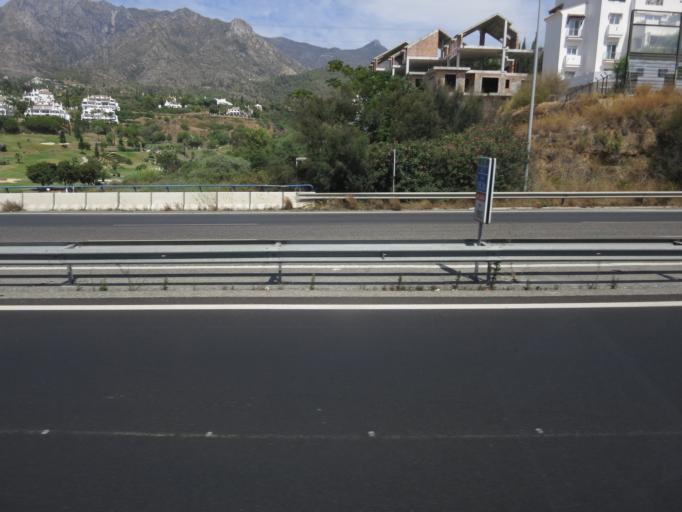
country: ES
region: Andalusia
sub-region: Provincia de Malaga
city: Marbella
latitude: 36.5163
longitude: -4.9029
